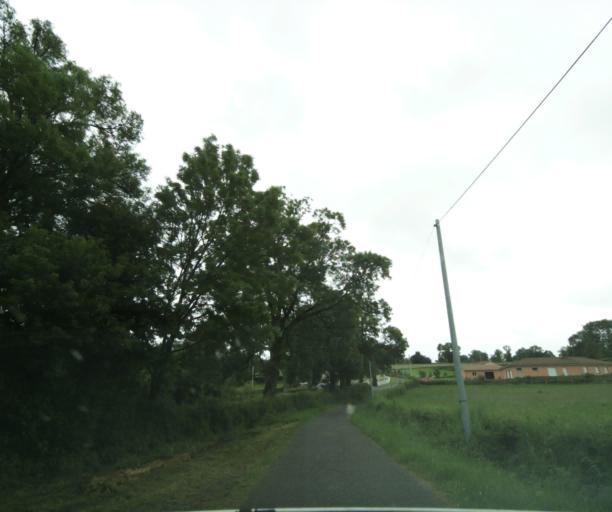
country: FR
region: Bourgogne
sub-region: Departement de Saone-et-Loire
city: Charolles
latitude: 46.4721
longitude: 4.3299
